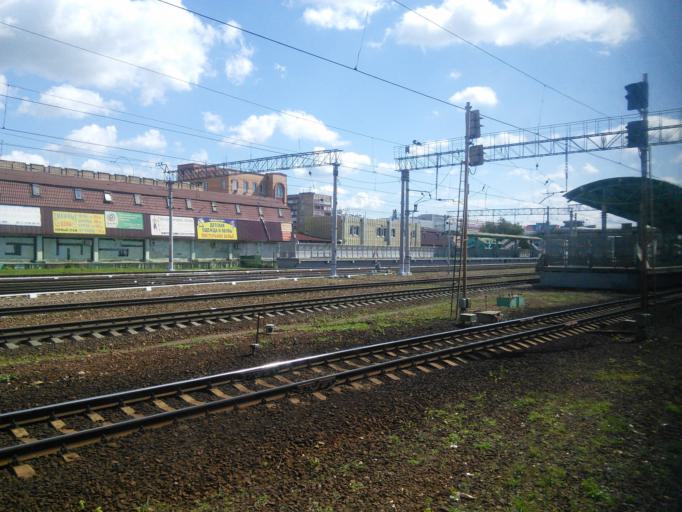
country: RU
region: Moskovskaya
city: Ramenskoye
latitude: 55.5661
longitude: 38.2231
